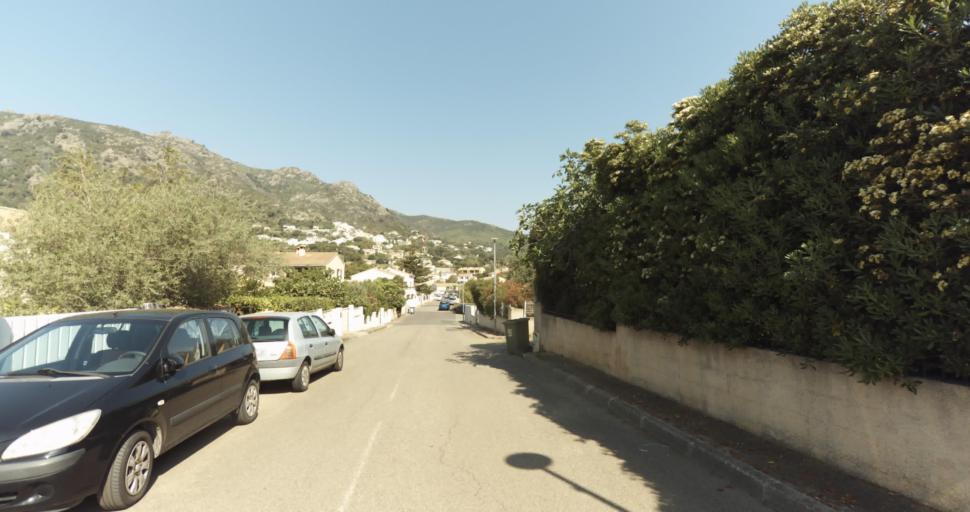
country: FR
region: Corsica
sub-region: Departement de la Haute-Corse
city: Biguglia
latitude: 42.6230
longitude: 9.4294
